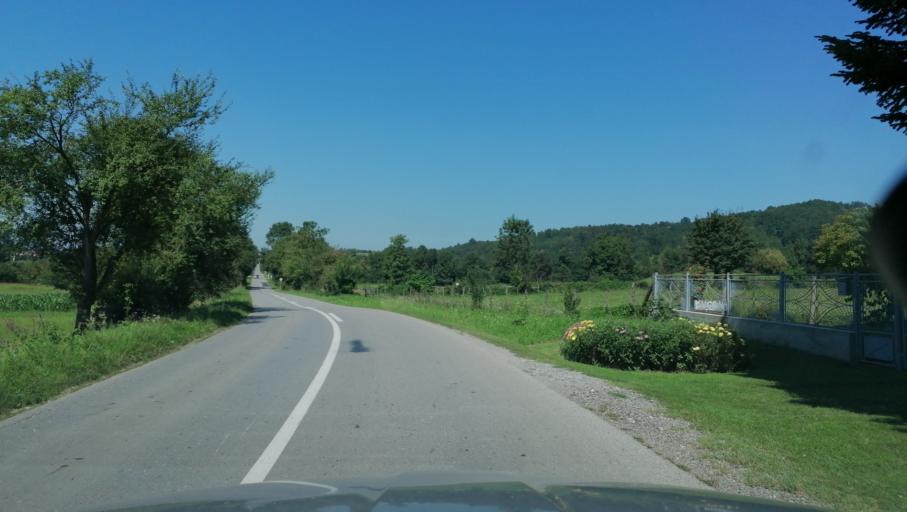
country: RS
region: Central Serbia
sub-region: Raski Okrug
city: Vrnjacka Banja
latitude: 43.6821
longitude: 20.8908
